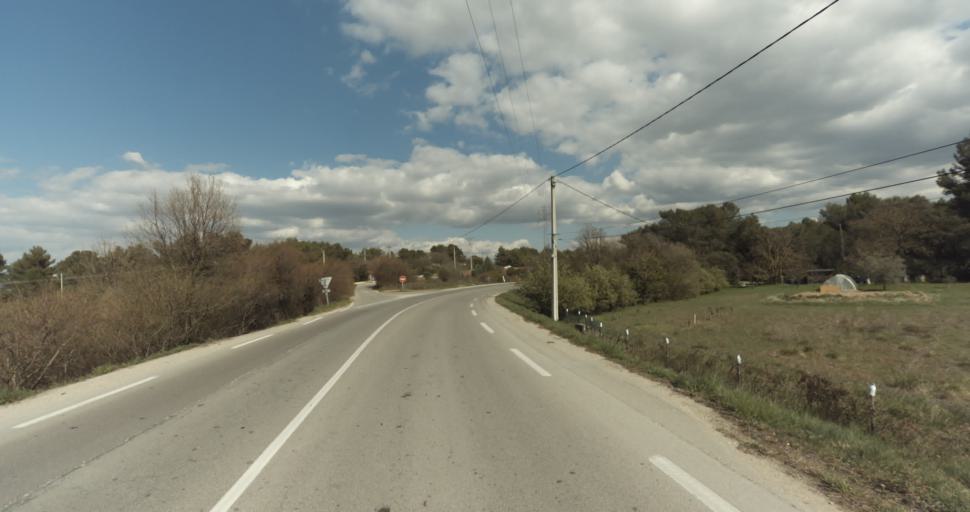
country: FR
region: Provence-Alpes-Cote d'Azur
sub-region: Departement des Bouches-du-Rhone
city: Greasque
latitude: 43.4459
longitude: 5.5216
